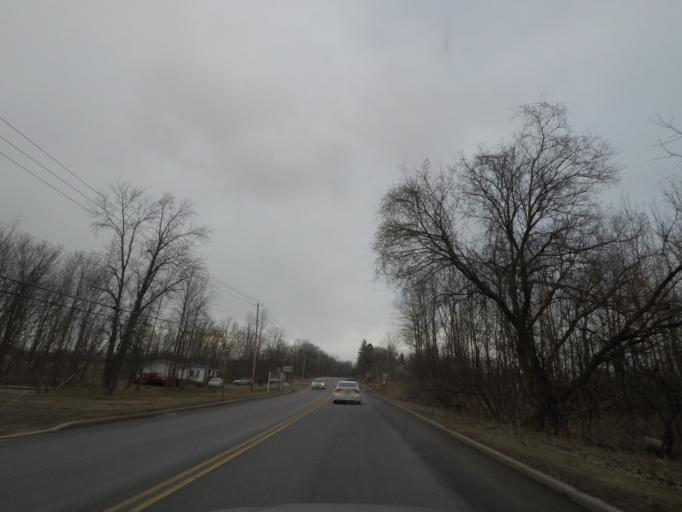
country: US
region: New York
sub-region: Oneida County
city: Sherrill
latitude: 43.0769
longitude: -75.6253
